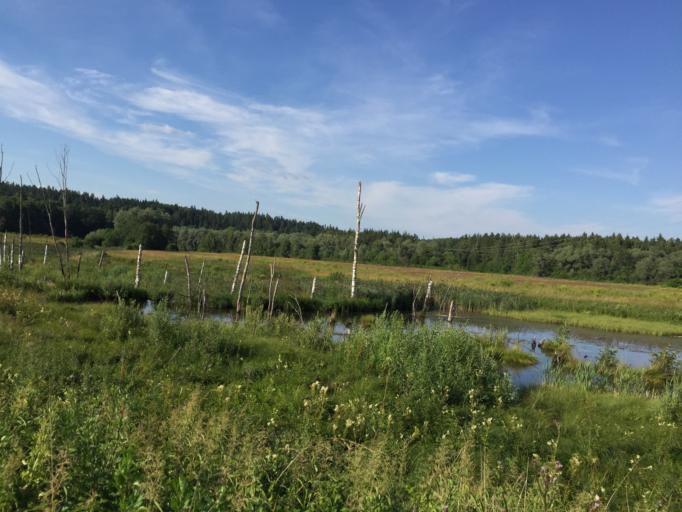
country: LV
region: Krimulda
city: Ragana
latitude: 57.1454
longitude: 24.7607
